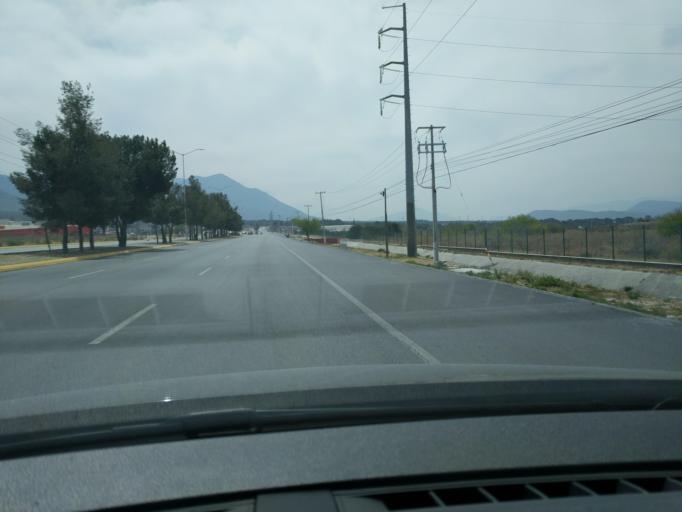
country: MX
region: Coahuila
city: Saltillo
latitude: 25.3564
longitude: -101.0207
